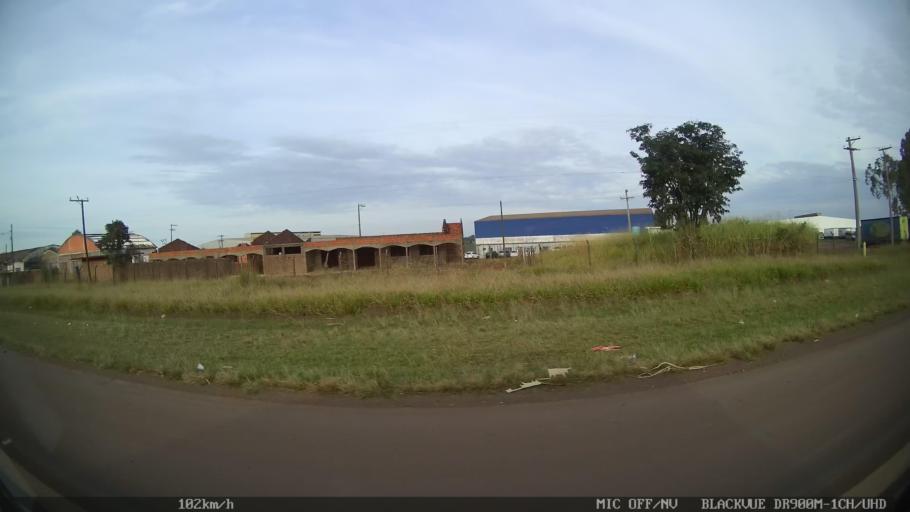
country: BR
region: Sao Paulo
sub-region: Iracemapolis
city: Iracemapolis
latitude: -22.6055
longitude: -47.4748
